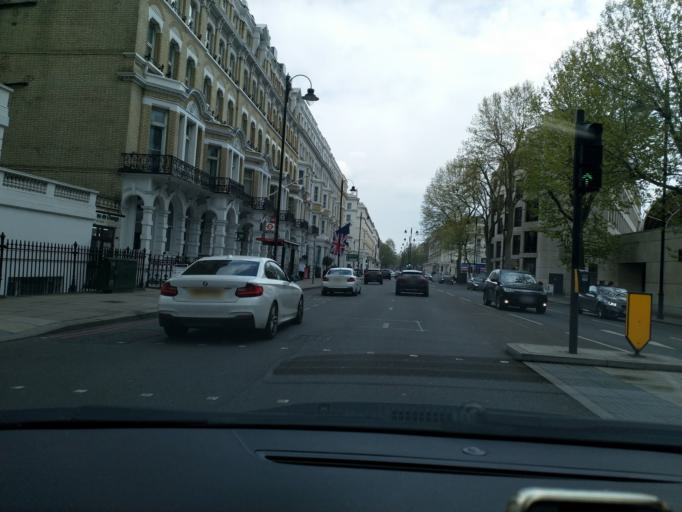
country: GB
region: England
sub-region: Greater London
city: Kensington
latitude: 51.4949
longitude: -0.1847
